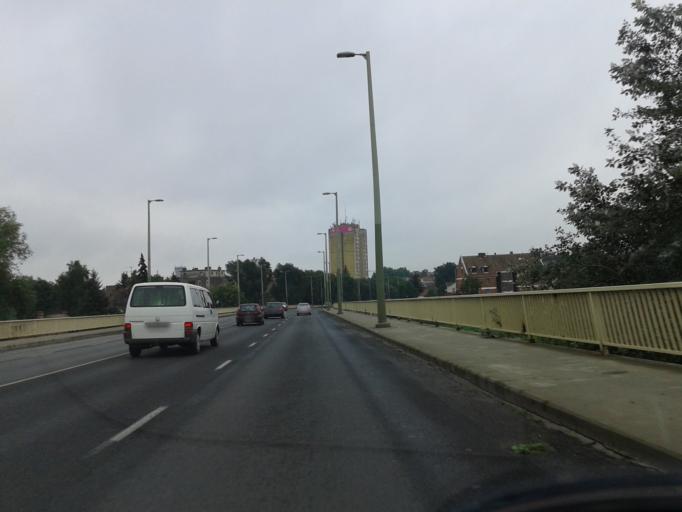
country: HU
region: Csongrad
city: Szeged
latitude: 46.2542
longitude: 20.1660
